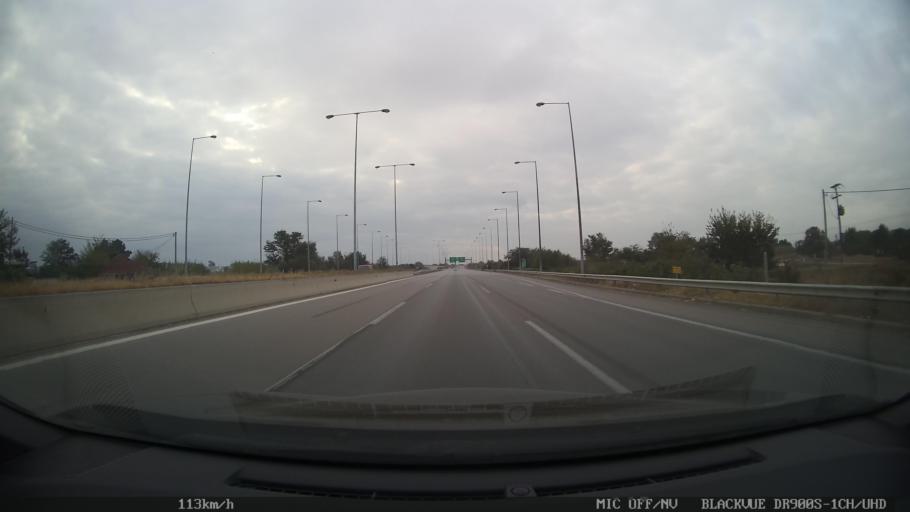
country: GR
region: Central Macedonia
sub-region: Nomos Thessalonikis
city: Kalochori
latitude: 40.6609
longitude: 22.8387
